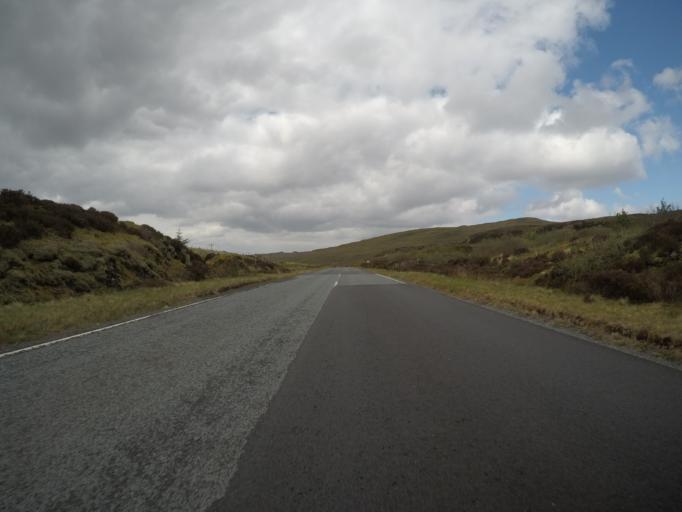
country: GB
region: Scotland
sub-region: Highland
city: Isle of Skye
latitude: 57.3161
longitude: -6.3208
